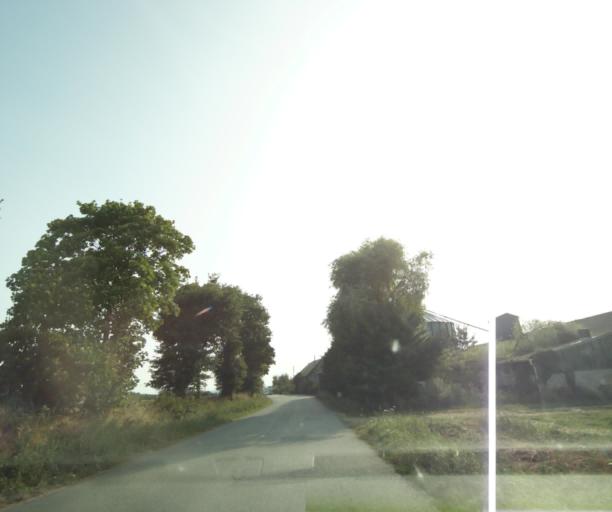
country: FR
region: Brittany
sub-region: Departement des Cotes-d'Armor
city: Jugon-les-Lacs
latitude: 48.4190
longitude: -2.3140
